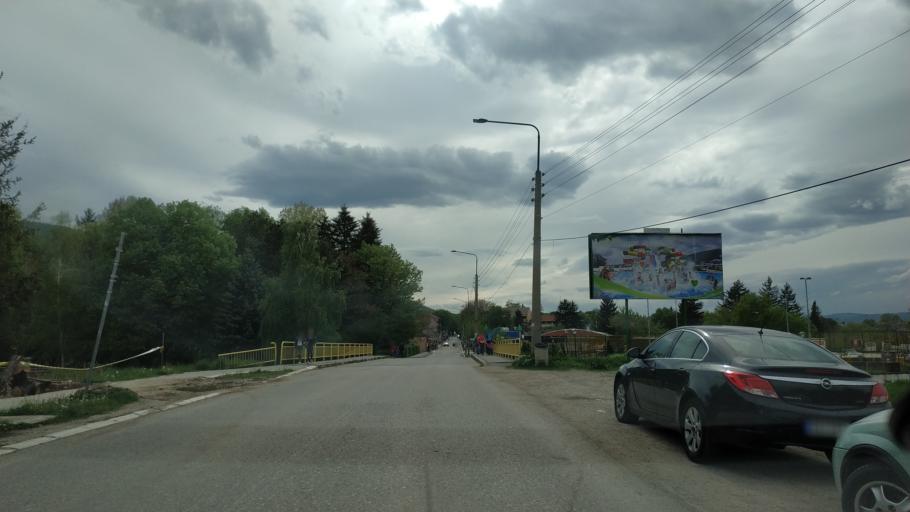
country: RS
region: Central Serbia
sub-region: Zajecarski Okrug
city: Soko Banja
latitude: 43.6455
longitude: 21.8816
